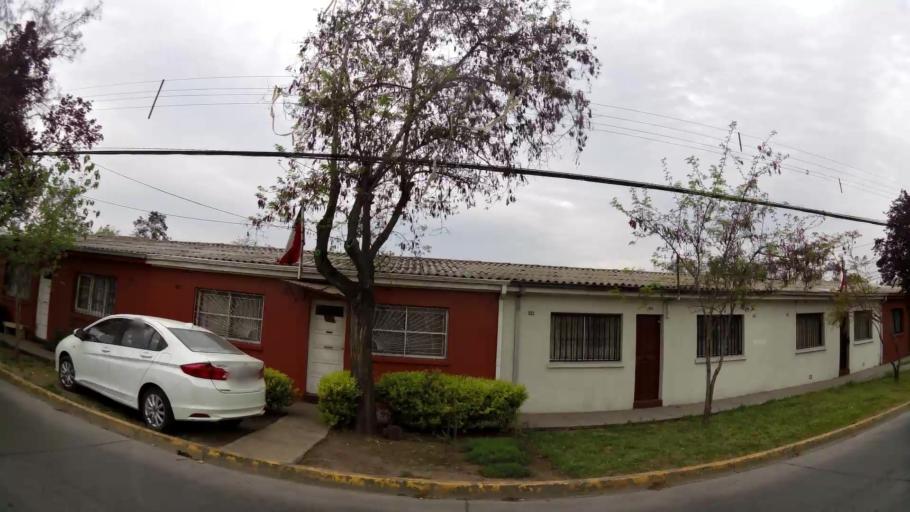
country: CL
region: Santiago Metropolitan
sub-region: Provincia de Santiago
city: Villa Presidente Frei, Nunoa, Santiago, Chile
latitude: -33.4718
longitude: -70.6135
